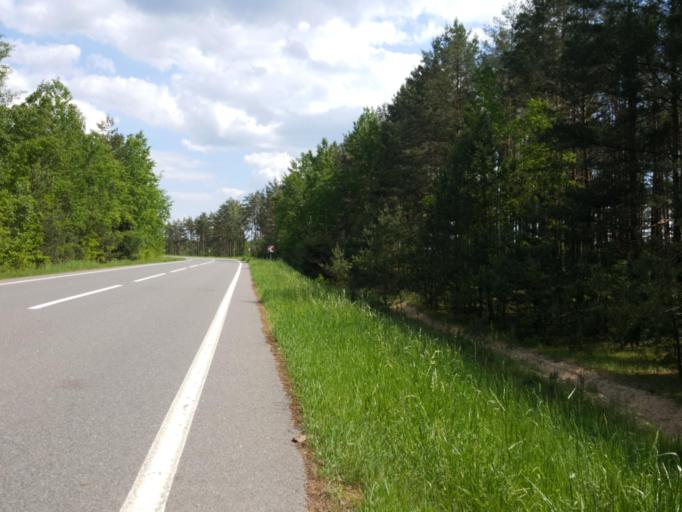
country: BY
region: Brest
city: Kamyanyuki
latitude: 52.5614
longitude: 23.6227
